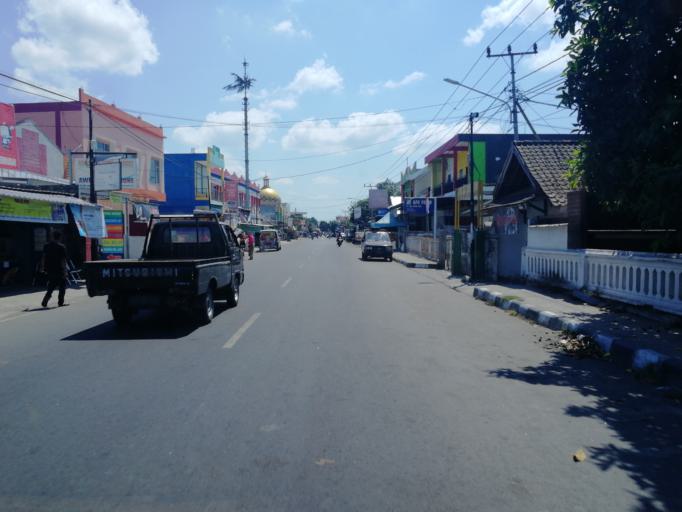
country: ID
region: West Nusa Tenggara
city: Kediri
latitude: -8.6879
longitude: 116.1212
